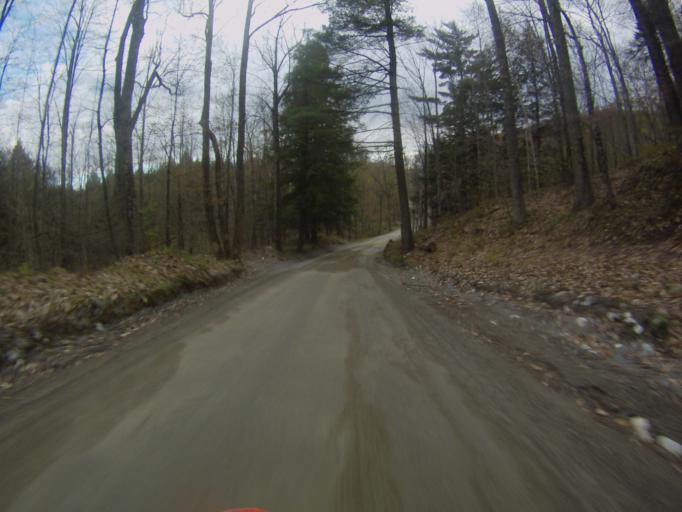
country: US
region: Vermont
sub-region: Addison County
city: Middlebury (village)
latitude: 43.9767
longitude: -73.0699
